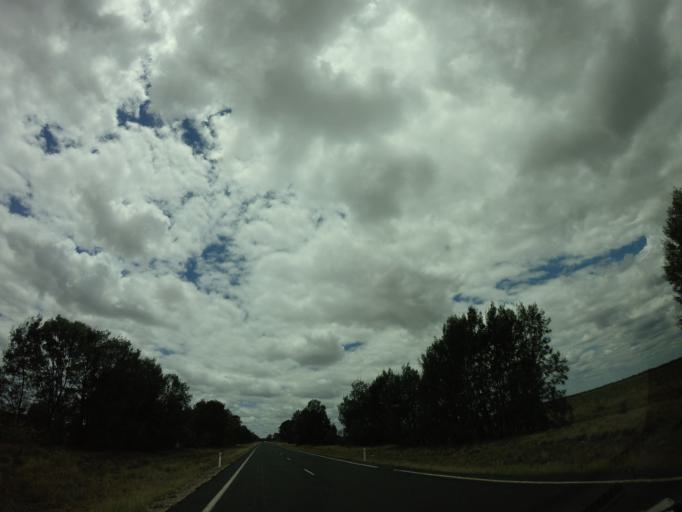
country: AU
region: Queensland
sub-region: Goondiwindi
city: Goondiwindi
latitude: -28.1668
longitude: 150.5260
